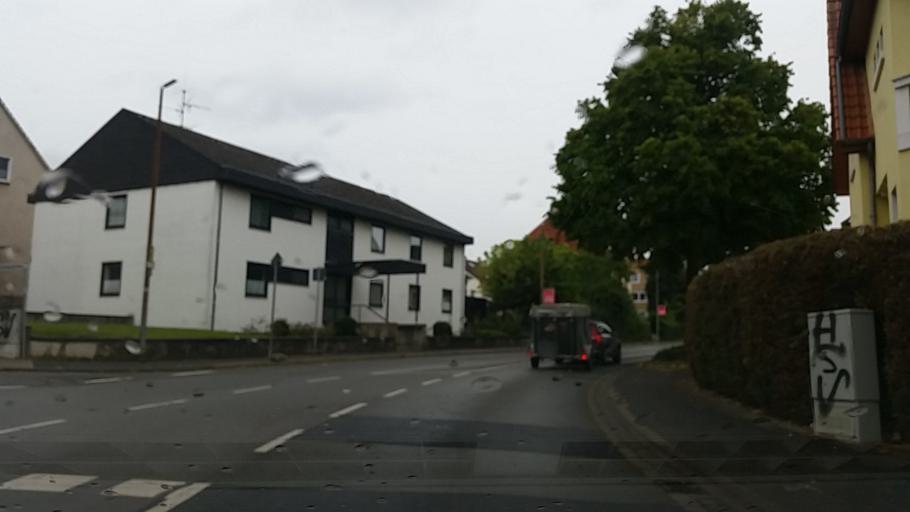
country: DE
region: Lower Saxony
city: Northeim
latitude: 51.7056
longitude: 10.0070
